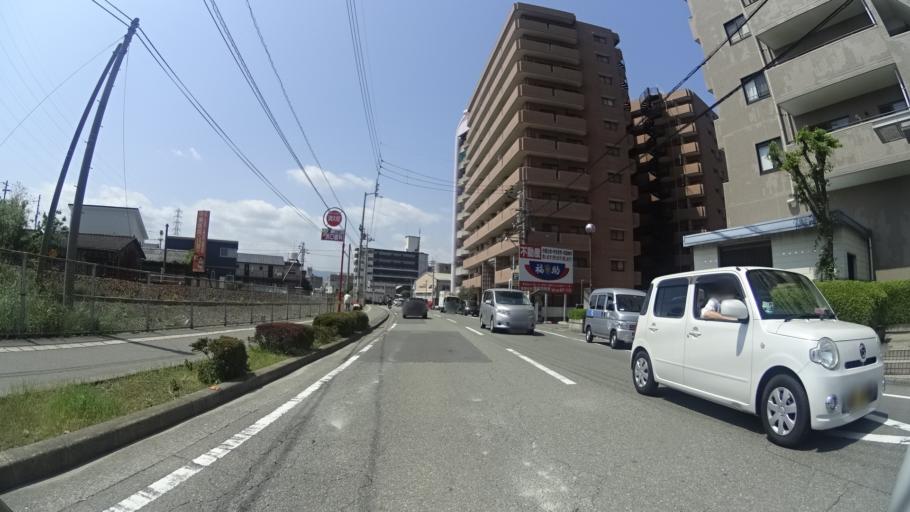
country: JP
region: Tokushima
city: Tokushima-shi
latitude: 34.0575
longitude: 134.5482
